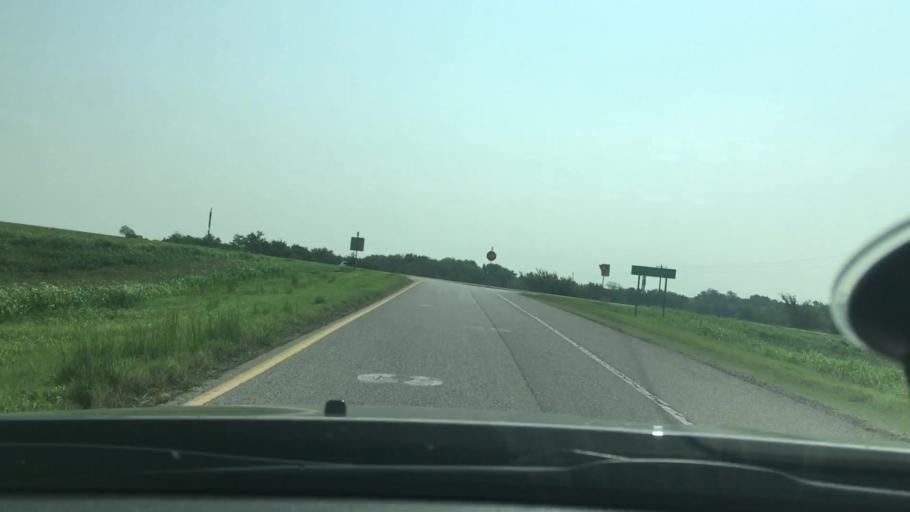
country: US
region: Oklahoma
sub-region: Pontotoc County
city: Ada
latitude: 34.6407
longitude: -96.5306
